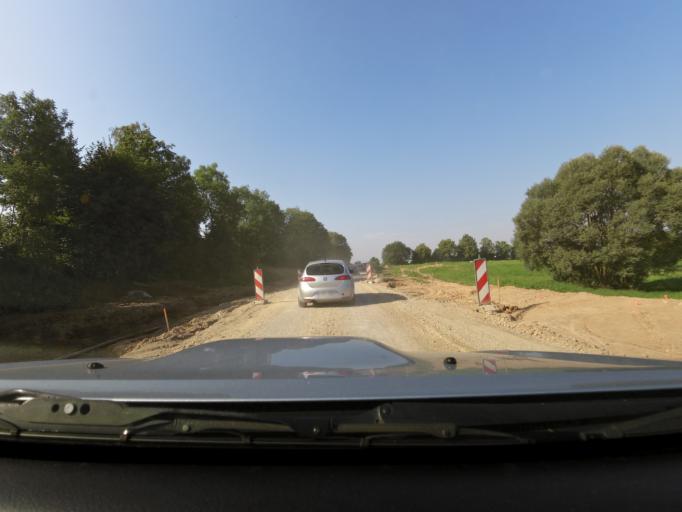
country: PL
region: Podlasie
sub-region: Powiat sejnenski
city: Sejny
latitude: 54.1061
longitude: 23.4096
